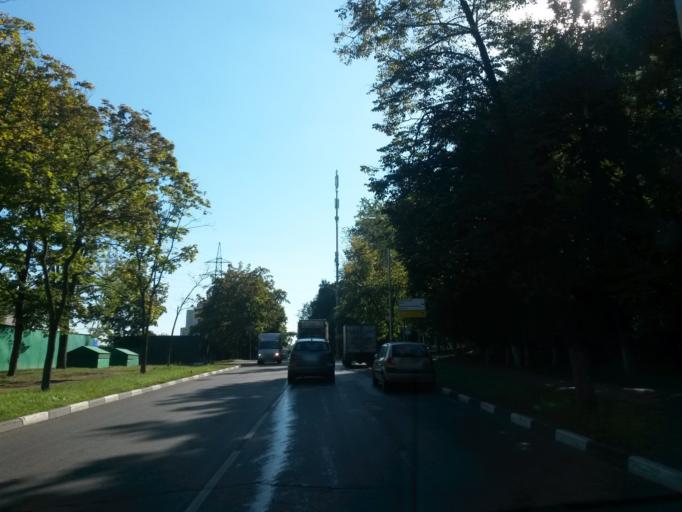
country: RU
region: Moscow
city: Kotlovka
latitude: 55.6591
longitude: 37.5867
